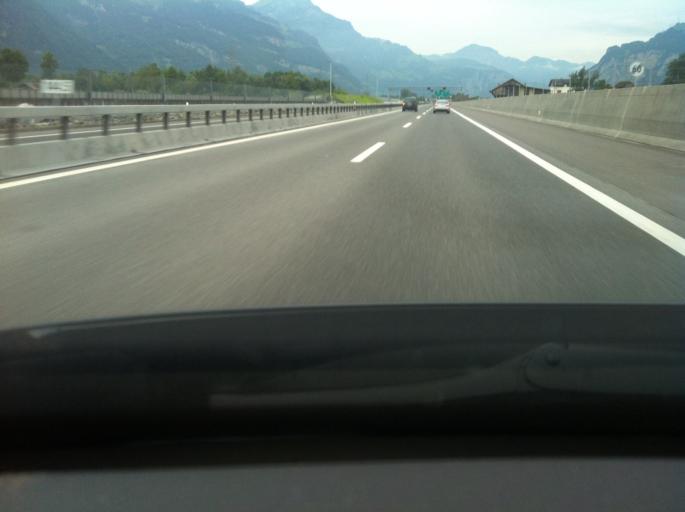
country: CH
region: Uri
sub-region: Uri
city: Seedorf
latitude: 46.8759
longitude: 8.6260
